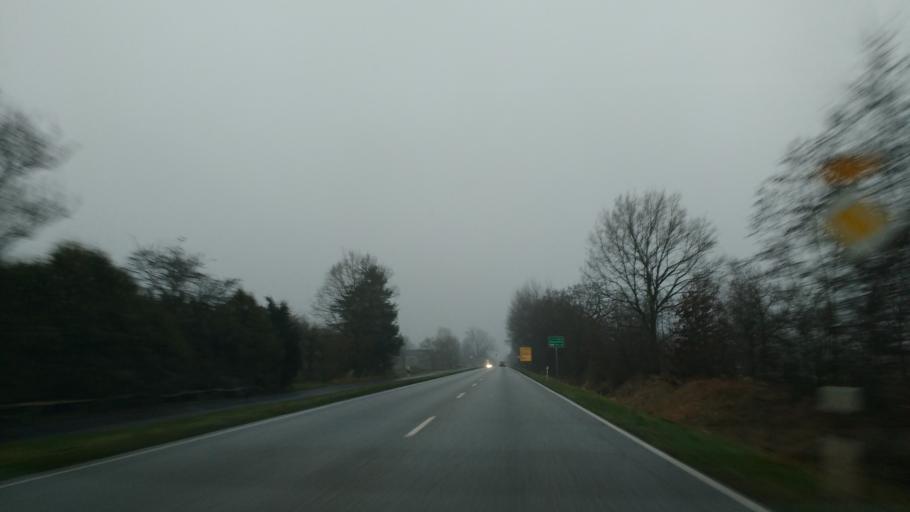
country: DE
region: Schleswig-Holstein
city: Brinjahe
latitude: 54.1868
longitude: 9.6392
